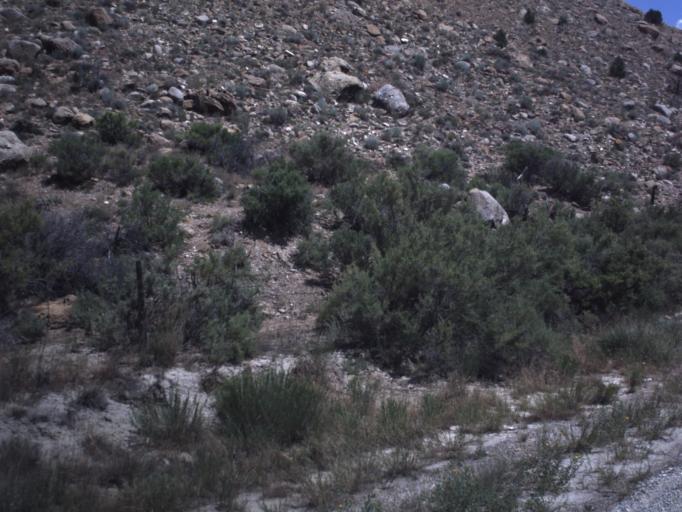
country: US
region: Utah
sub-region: Emery County
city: Orangeville
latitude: 39.2632
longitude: -111.1226
